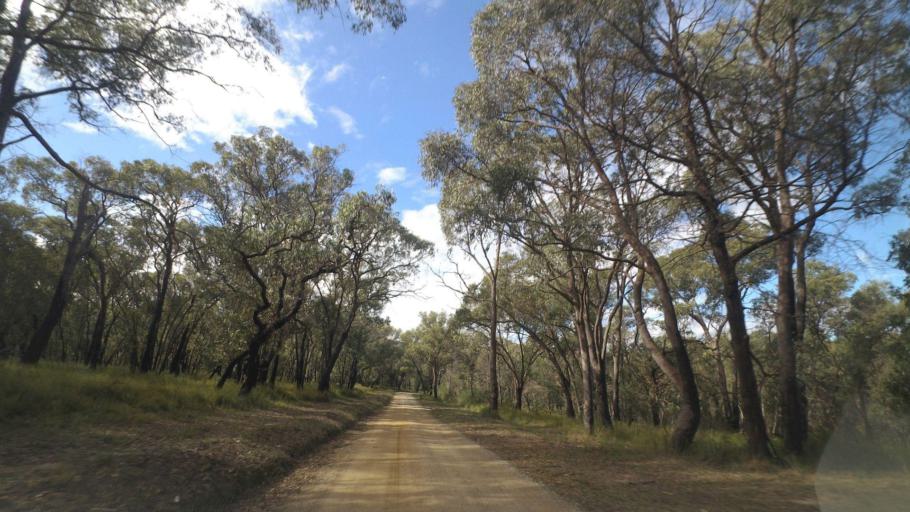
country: AU
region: Victoria
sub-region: Cardinia
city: Gembrook
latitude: -37.9874
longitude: 145.6384
